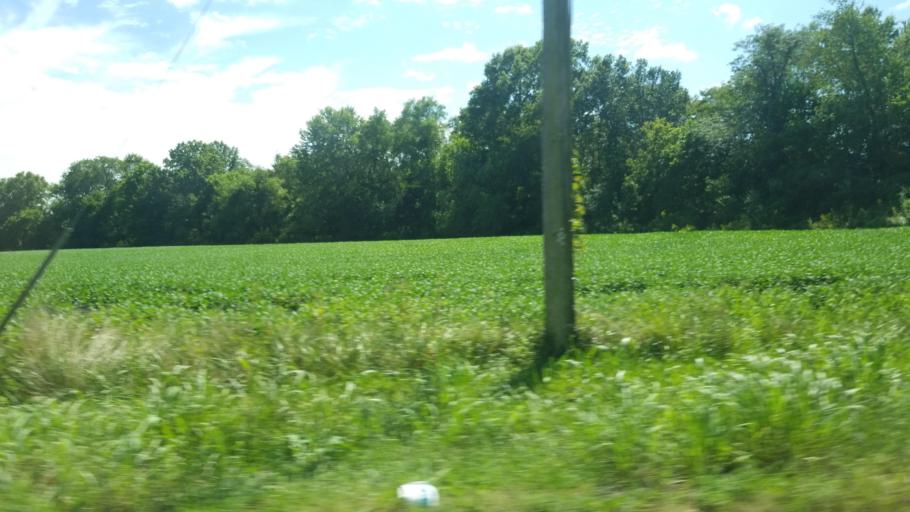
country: US
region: Illinois
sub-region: Williamson County
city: Johnston City
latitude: 37.7893
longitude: -88.9225
